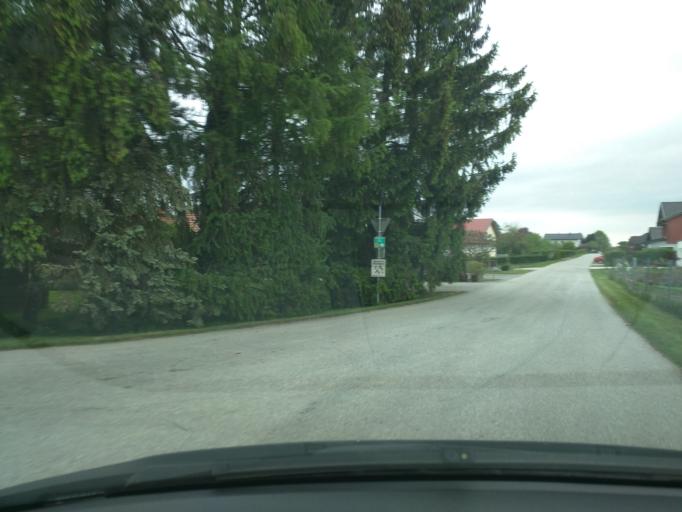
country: AT
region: Lower Austria
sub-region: Politischer Bezirk Amstetten
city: Sankt Georgen am Ybbsfelde
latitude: 48.1155
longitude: 14.9636
